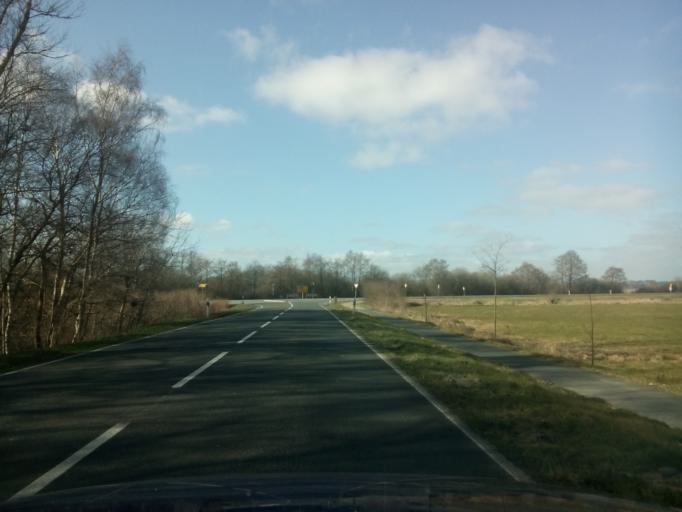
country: DE
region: Lower Saxony
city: Osterholz-Scharmbeck
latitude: 53.1936
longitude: 8.8229
